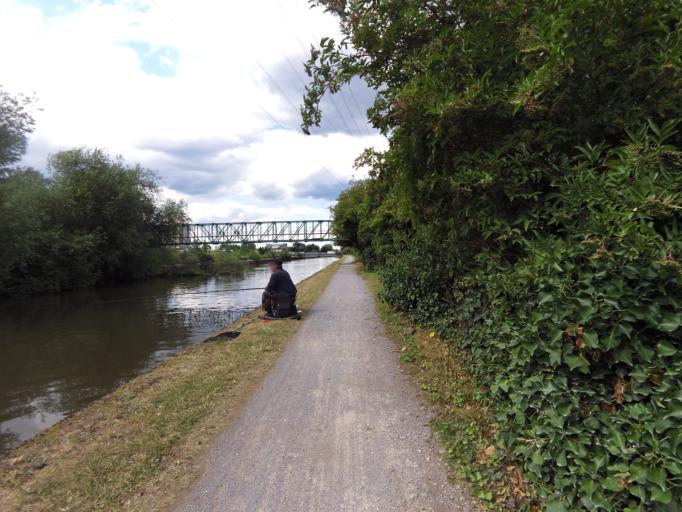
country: GB
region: England
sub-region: Greater London
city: Walthamstow
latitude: 51.6370
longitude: -0.0306
